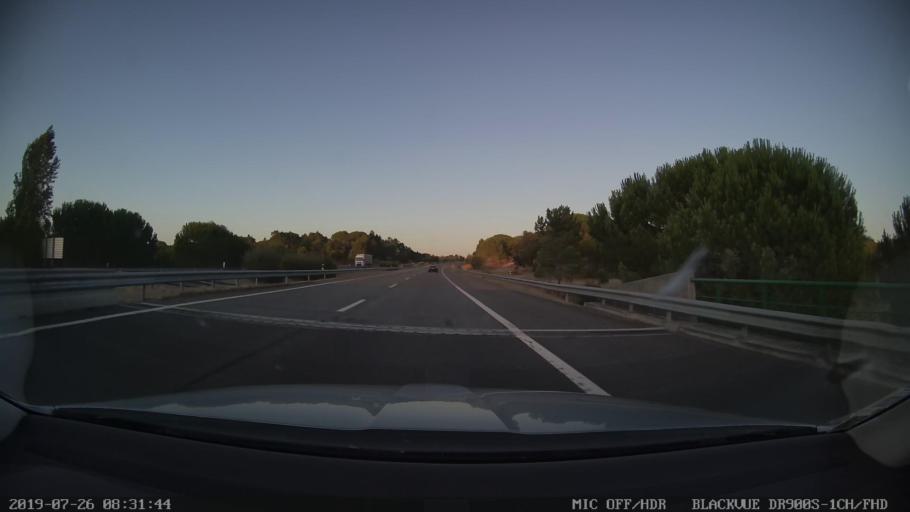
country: PT
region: Evora
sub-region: Vendas Novas
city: Vendas Novas
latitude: 38.6325
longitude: -8.5391
